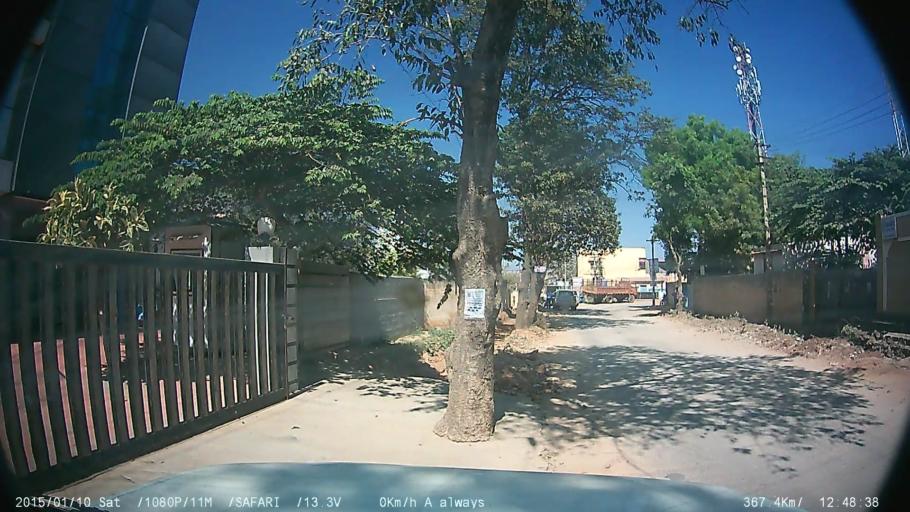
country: IN
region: Tamil Nadu
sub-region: Krishnagiri
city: Hosur
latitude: 12.7725
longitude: 77.7977
